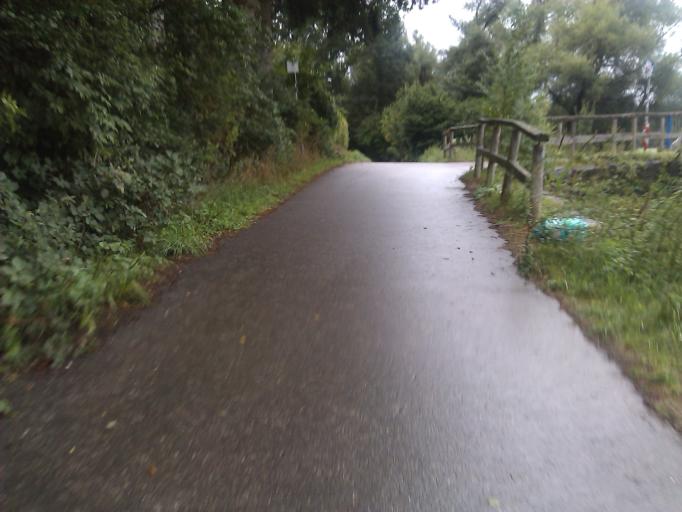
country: DE
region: Baden-Wuerttemberg
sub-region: Tuebingen Region
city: Pliezhausen
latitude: 48.5587
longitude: 9.2199
